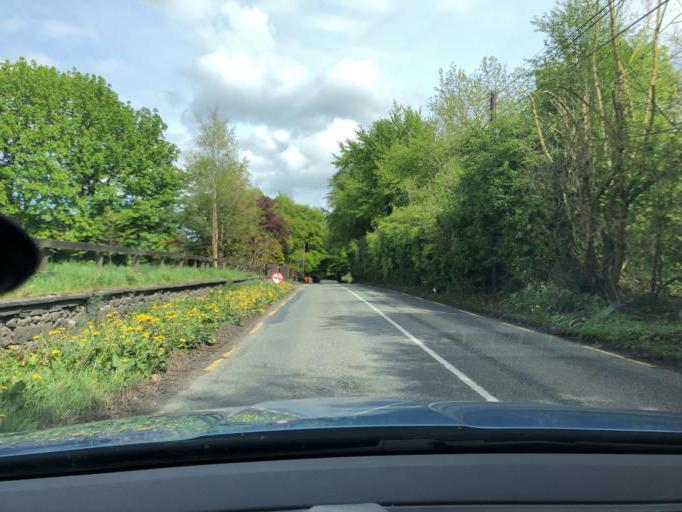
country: IE
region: Leinster
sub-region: Laois
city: Abbeyleix
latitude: 52.9082
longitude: -7.3833
